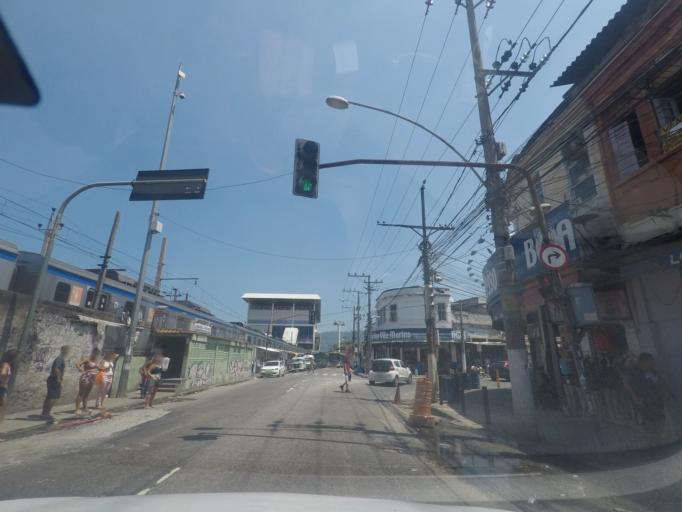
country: BR
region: Rio de Janeiro
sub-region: Rio De Janeiro
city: Rio de Janeiro
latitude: -22.8661
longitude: -43.2560
